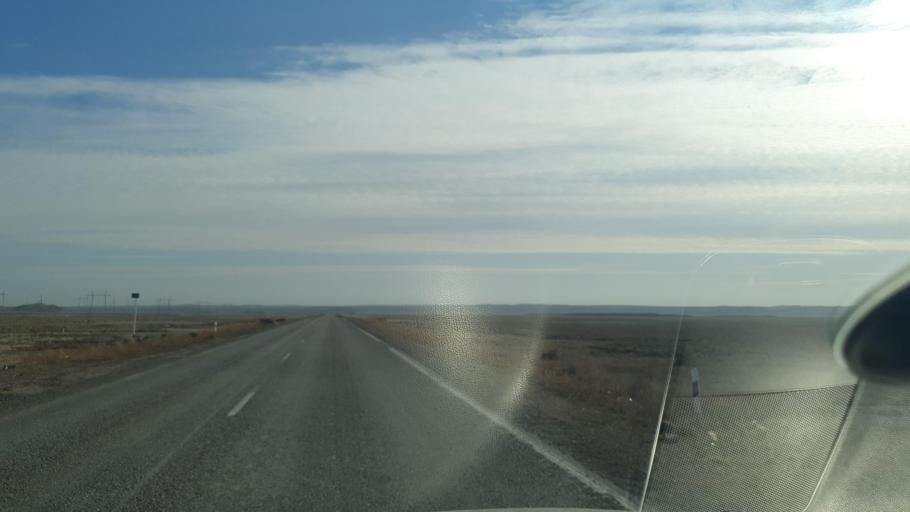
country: KZ
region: Zhambyl
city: Mynaral
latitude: 45.5854
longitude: 73.4057
